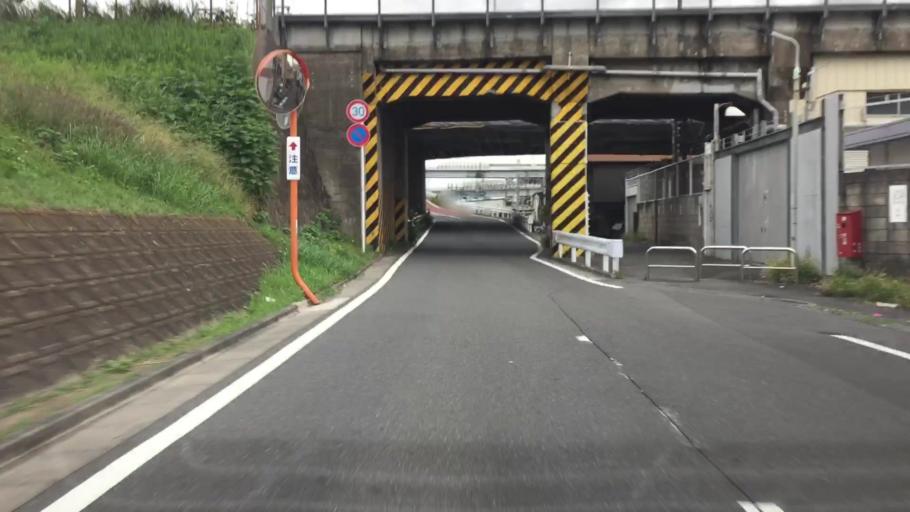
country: JP
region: Saitama
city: Soka
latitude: 35.7453
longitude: 139.8164
